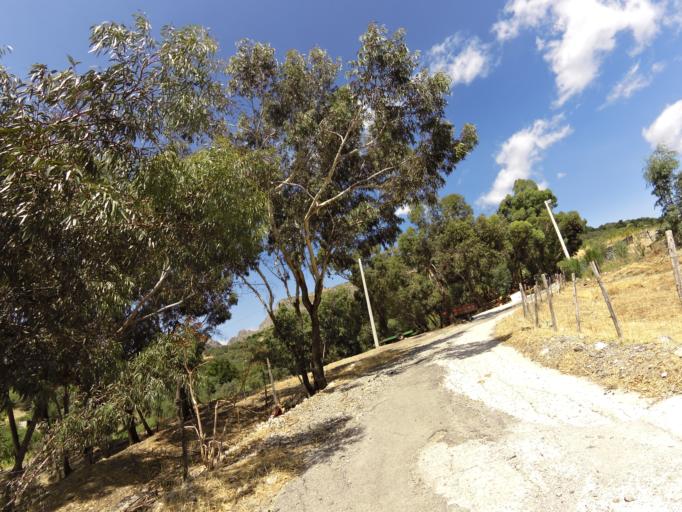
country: IT
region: Calabria
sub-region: Provincia di Reggio Calabria
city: Stilo
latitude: 38.4741
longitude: 16.4787
